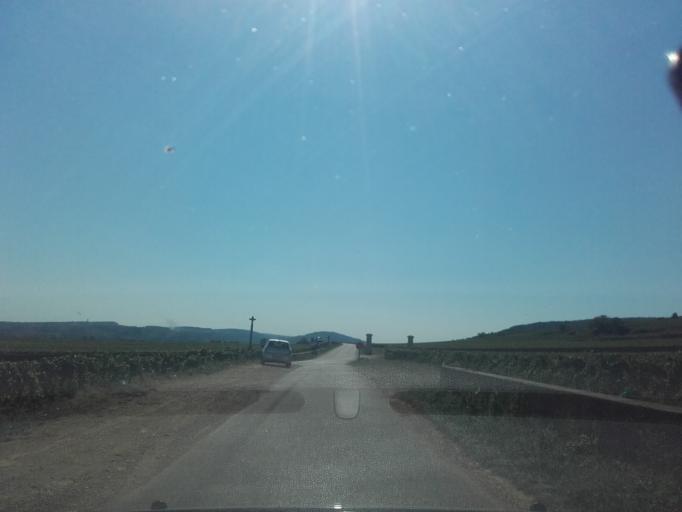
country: FR
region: Bourgogne
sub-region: Departement de la Cote-d'Or
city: Corpeau
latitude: 46.9477
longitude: 4.7412
